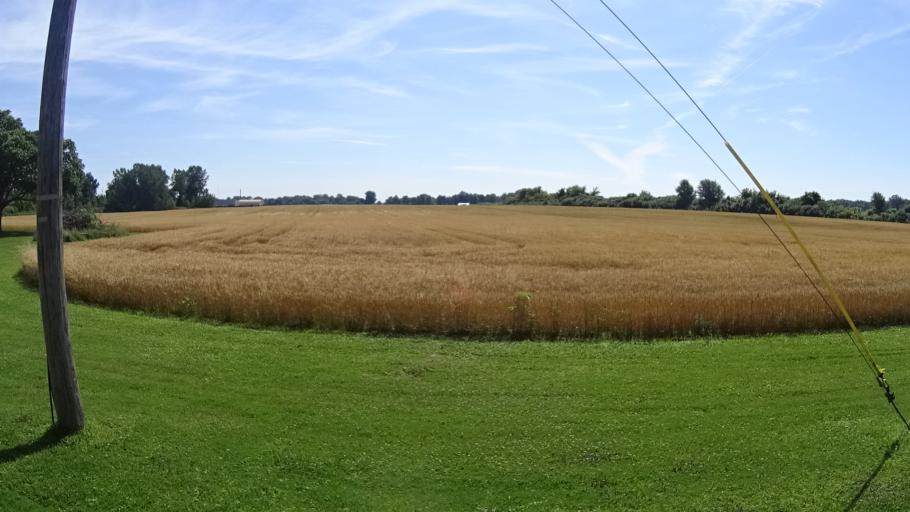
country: US
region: Ohio
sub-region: Erie County
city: Huron
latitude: 41.3769
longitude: -82.4721
